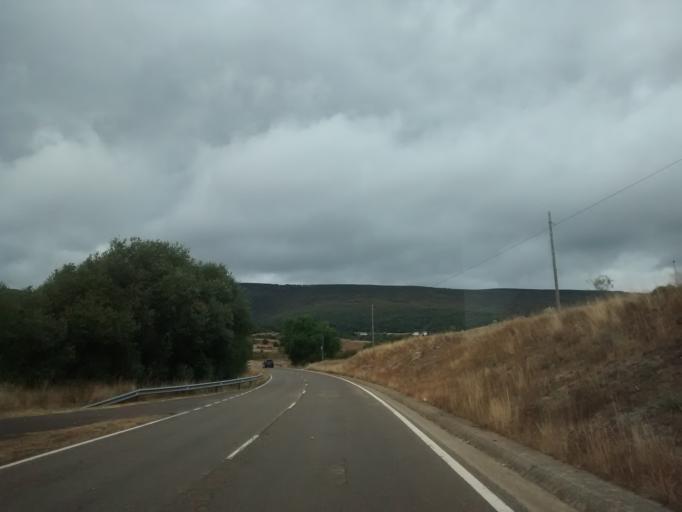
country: ES
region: Cantabria
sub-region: Provincia de Cantabria
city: Mataporquera
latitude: 42.8958
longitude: -4.0782
